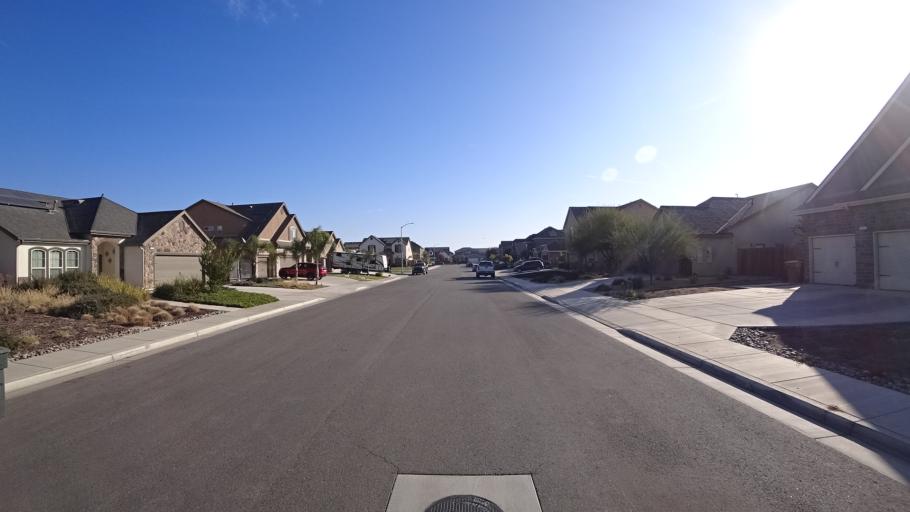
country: US
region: California
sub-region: Kern County
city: Greenfield
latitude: 35.2689
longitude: -119.0701
